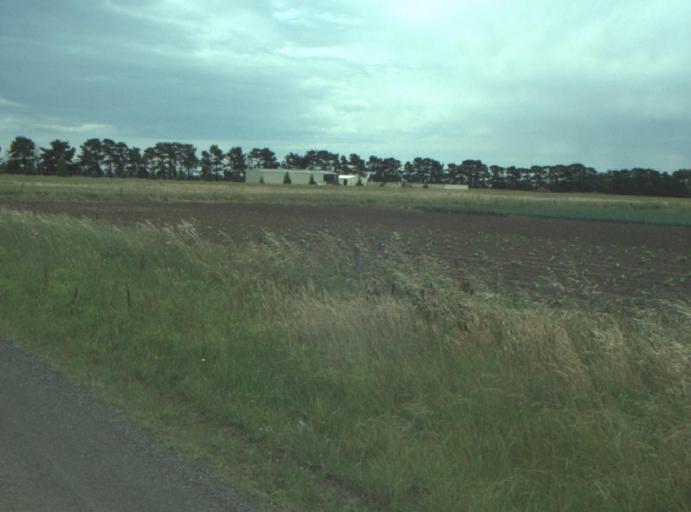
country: AU
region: Victoria
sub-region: Greater Geelong
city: Leopold
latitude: -38.2058
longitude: 144.4517
